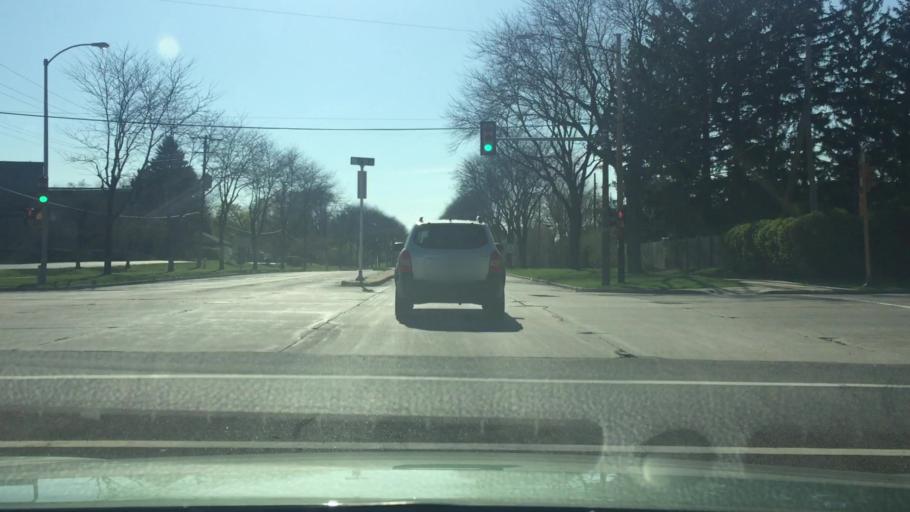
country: US
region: Wisconsin
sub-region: Milwaukee County
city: Brown Deer
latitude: 43.1632
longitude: -87.9747
